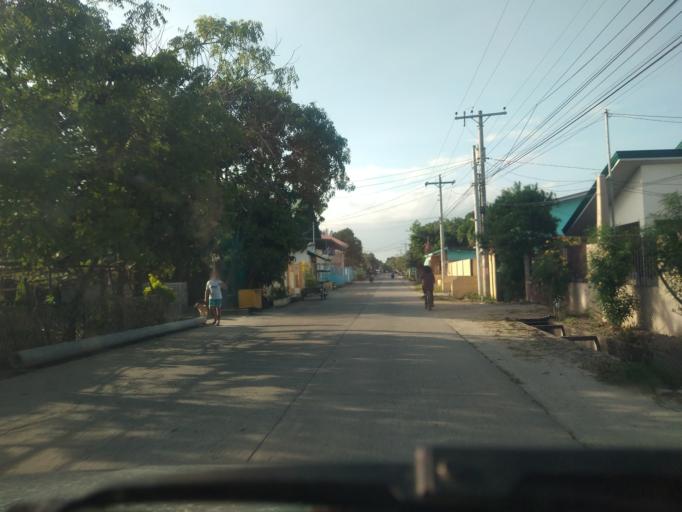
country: PH
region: Central Luzon
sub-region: Province of Pampanga
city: Bulaon
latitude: 15.0940
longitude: 120.6841
